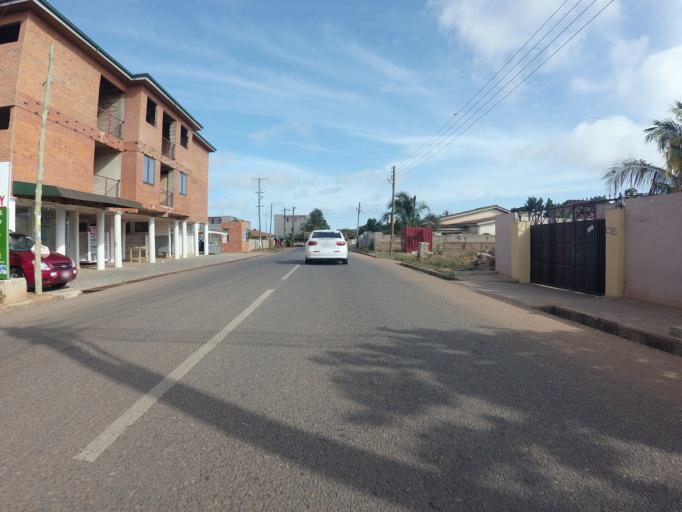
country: GH
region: Greater Accra
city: Teshi Old Town
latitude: 5.5833
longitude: -0.1420
